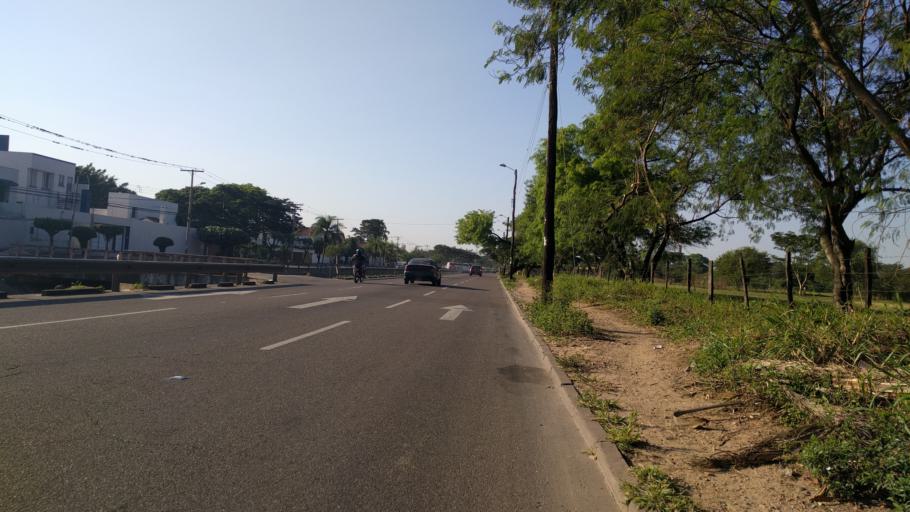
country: BO
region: Santa Cruz
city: Santa Cruz de la Sierra
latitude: -17.8080
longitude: -63.1634
